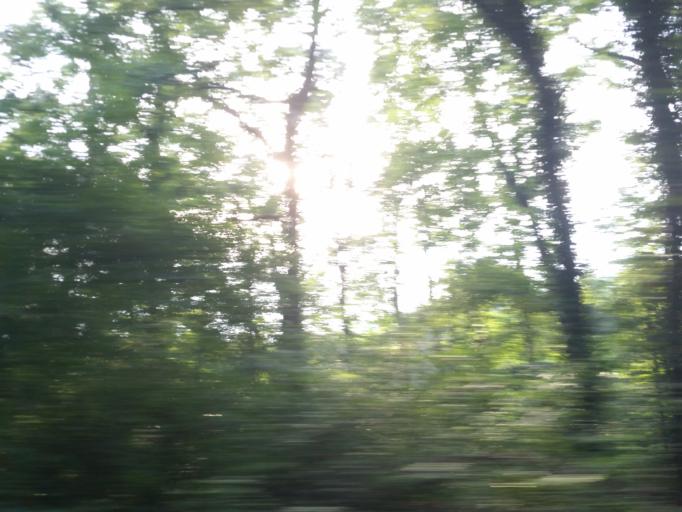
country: US
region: Tennessee
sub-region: Knox County
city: Knoxville
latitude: 36.0443
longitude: -83.9471
